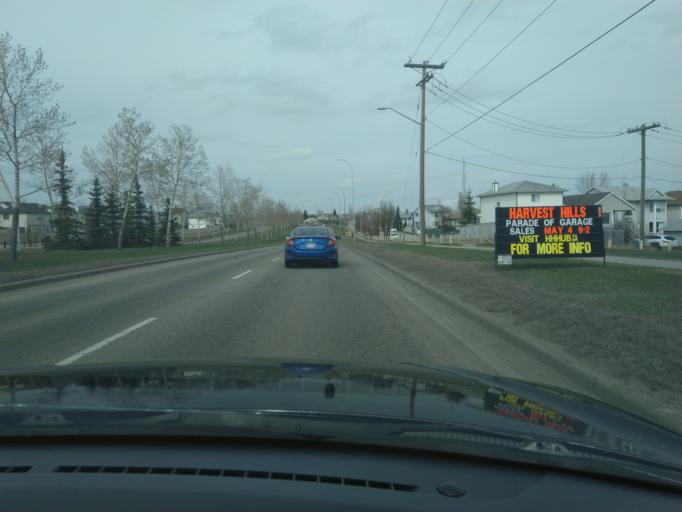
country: CA
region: Alberta
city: Calgary
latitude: 51.1437
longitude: -114.0671
